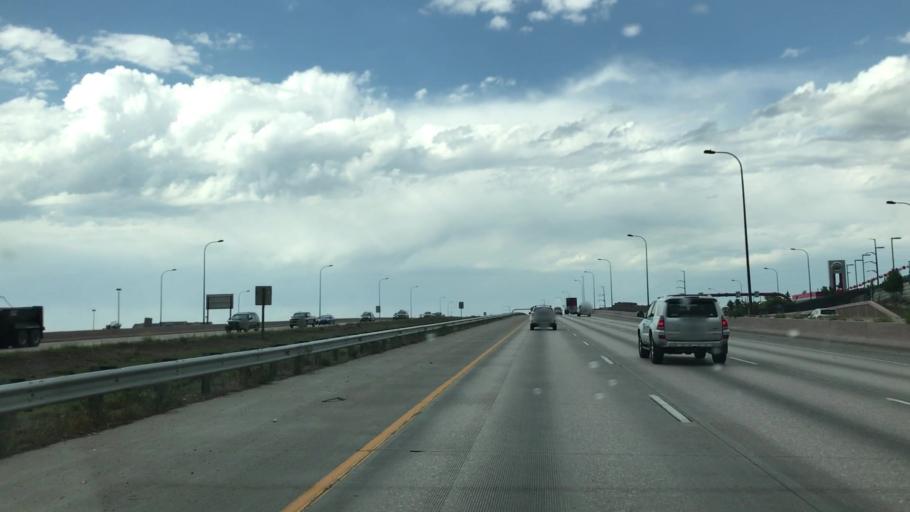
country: US
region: Colorado
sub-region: El Paso County
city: Air Force Academy
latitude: 38.9296
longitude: -104.8117
